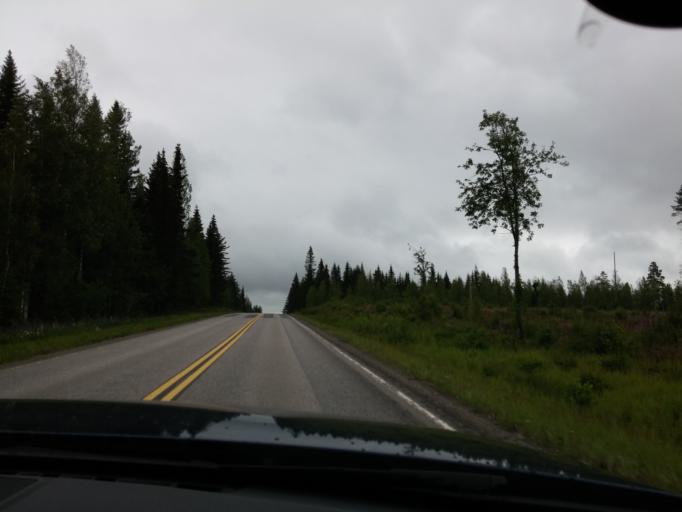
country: FI
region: Central Finland
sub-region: Keuruu
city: Keuruu
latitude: 62.3249
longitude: 24.7338
